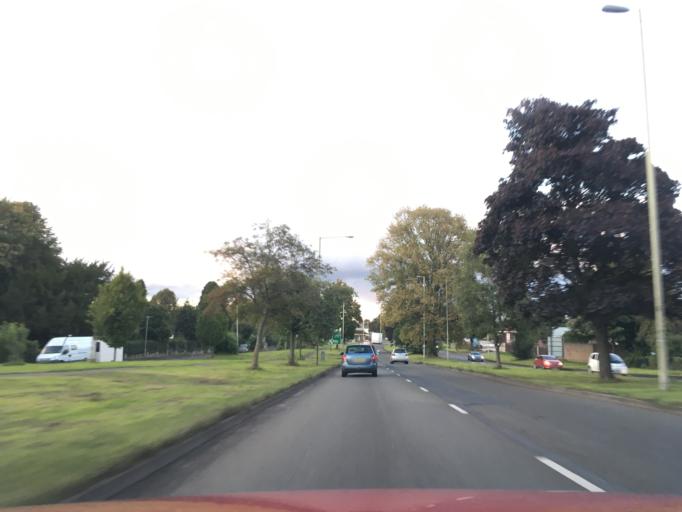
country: GB
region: England
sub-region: Gloucestershire
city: Gloucester
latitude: 51.8484
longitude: -2.2273
